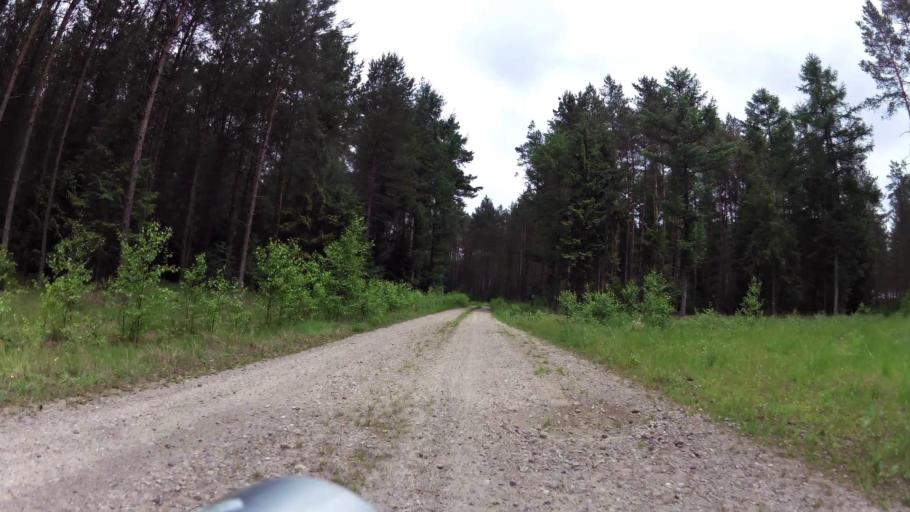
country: PL
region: West Pomeranian Voivodeship
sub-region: Powiat szczecinecki
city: Bialy Bor
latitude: 53.9183
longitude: 16.8307
